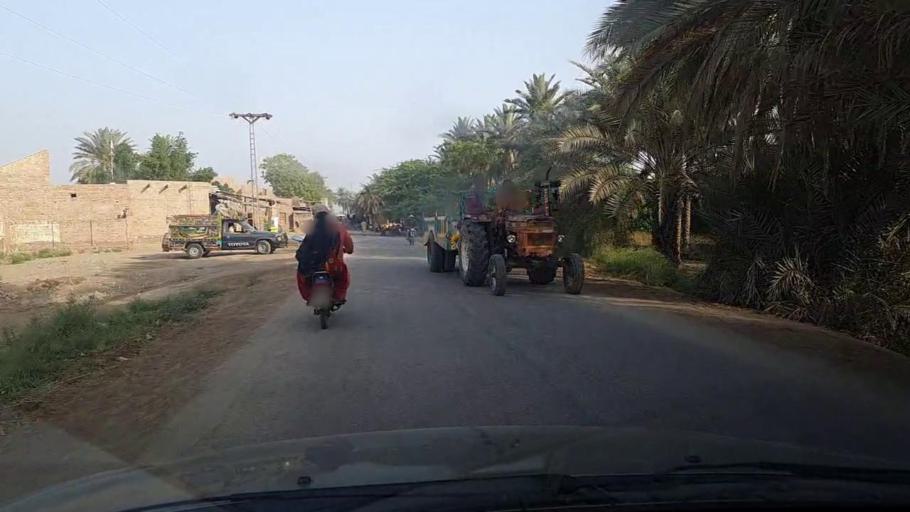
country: PK
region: Sindh
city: Pir jo Goth
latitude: 27.5571
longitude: 68.6758
